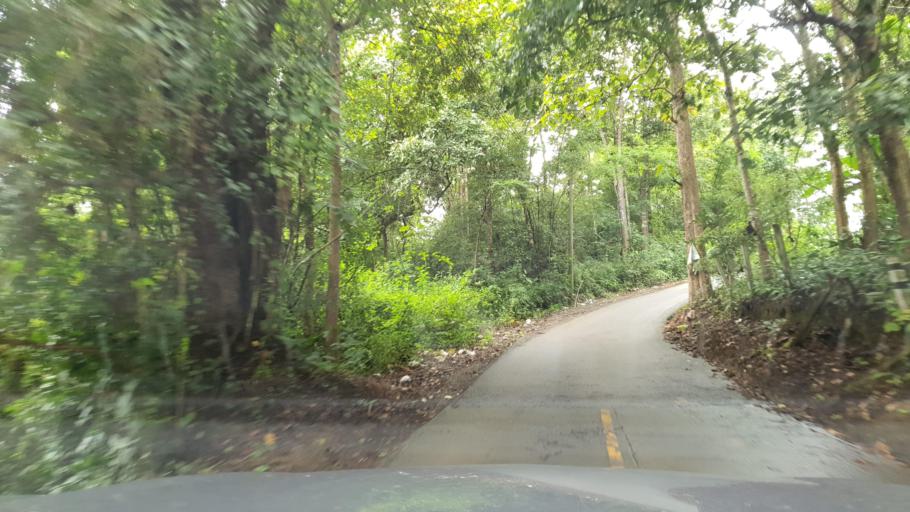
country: TH
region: Chiang Mai
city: Mae Taeng
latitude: 19.2004
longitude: 98.9369
